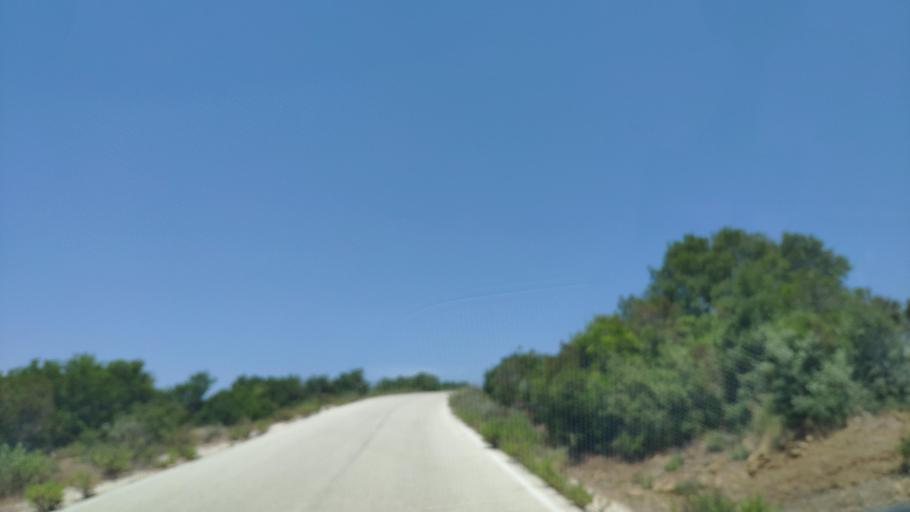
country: GR
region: West Greece
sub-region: Nomos Aitolias kai Akarnanias
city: Sardinia
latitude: 38.8796
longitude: 21.2792
